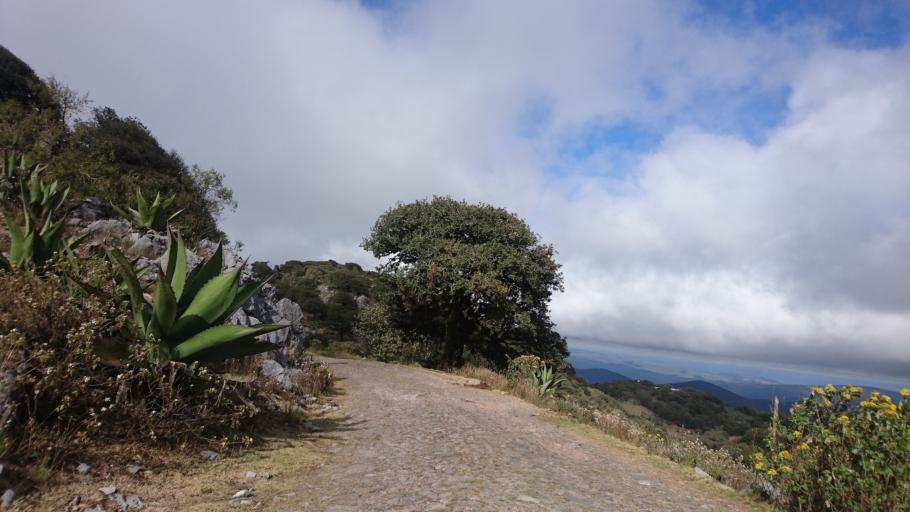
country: MX
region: San Luis Potosi
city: Zaragoza
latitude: 22.0692
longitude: -100.6419
